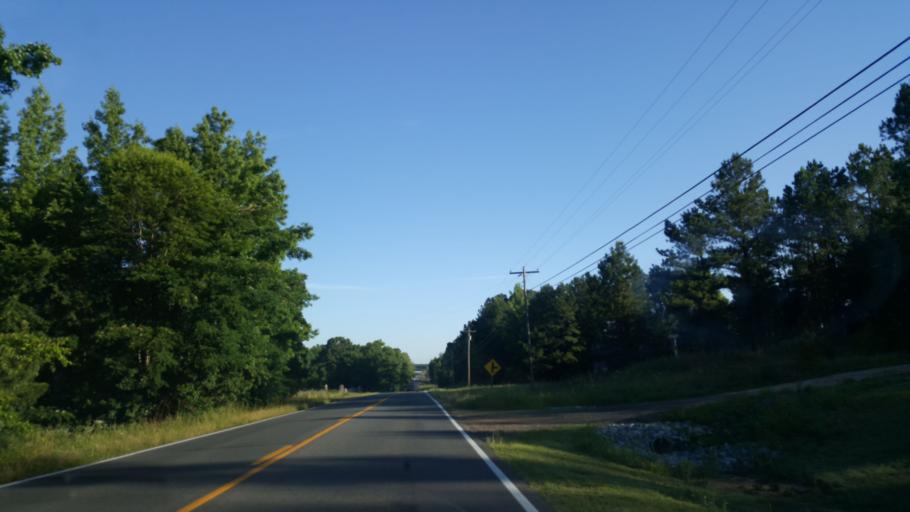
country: US
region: Tennessee
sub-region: Henderson County
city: Lexington
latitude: 35.6109
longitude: -88.3982
